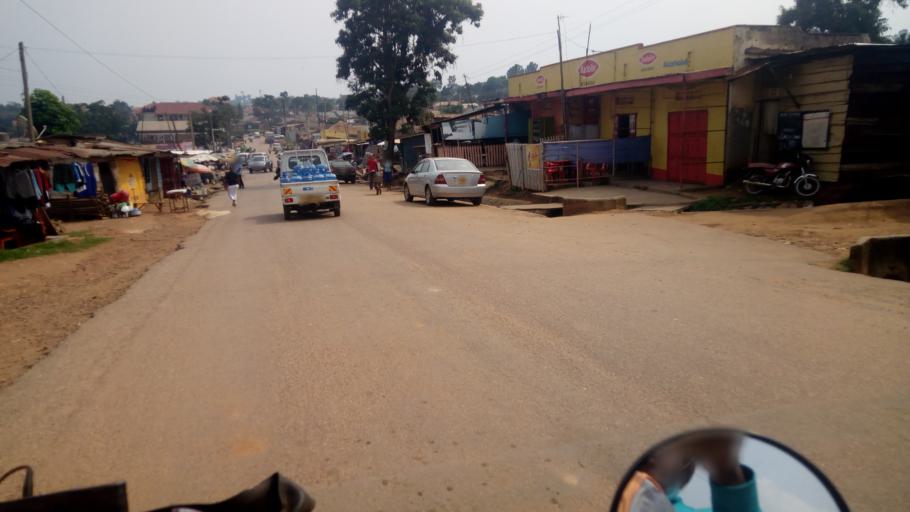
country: UG
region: Central Region
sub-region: Wakiso District
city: Kireka
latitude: 0.3067
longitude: 32.6544
